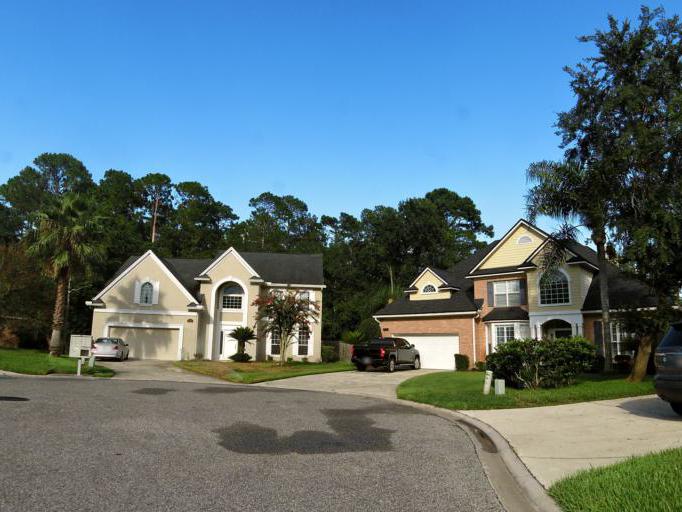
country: US
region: Florida
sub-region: Saint Johns County
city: Fruit Cove
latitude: 30.2125
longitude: -81.5333
